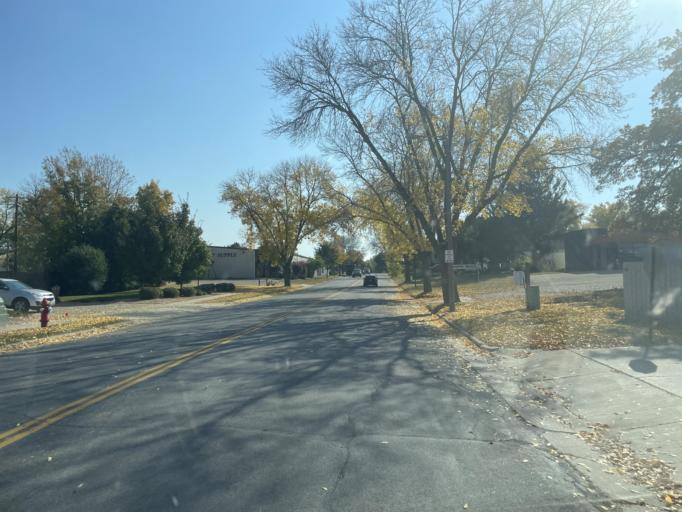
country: US
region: Wisconsin
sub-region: Dane County
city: Madison
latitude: 43.0313
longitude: -89.4050
